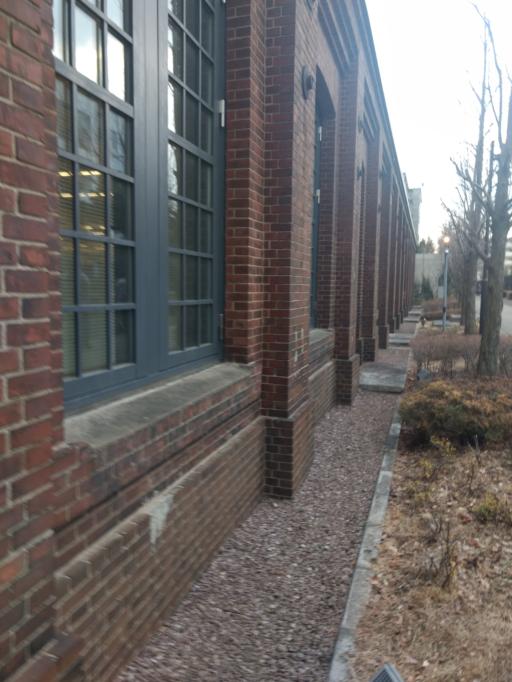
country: JP
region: Saitama
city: Kawaguchi
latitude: 35.7565
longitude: 139.7287
